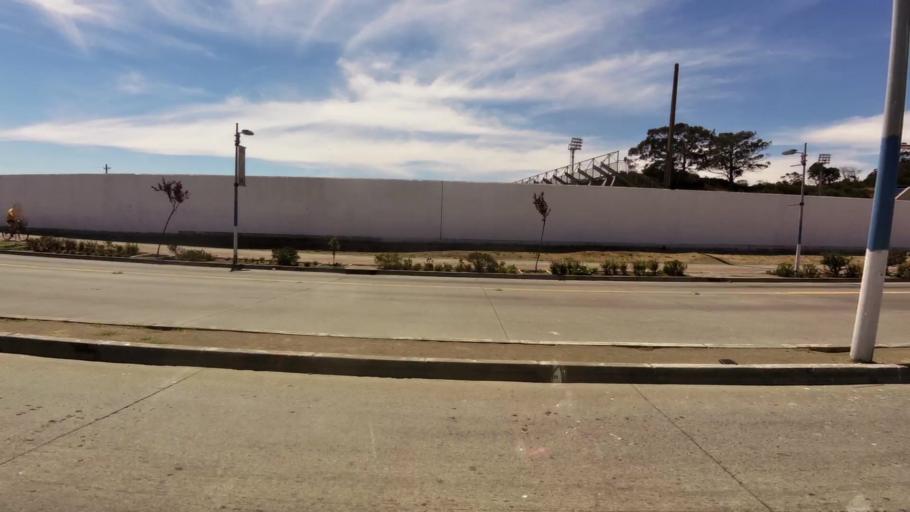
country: CL
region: Biobio
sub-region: Provincia de Concepcion
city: Talcahuano
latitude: -36.7224
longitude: -73.1086
